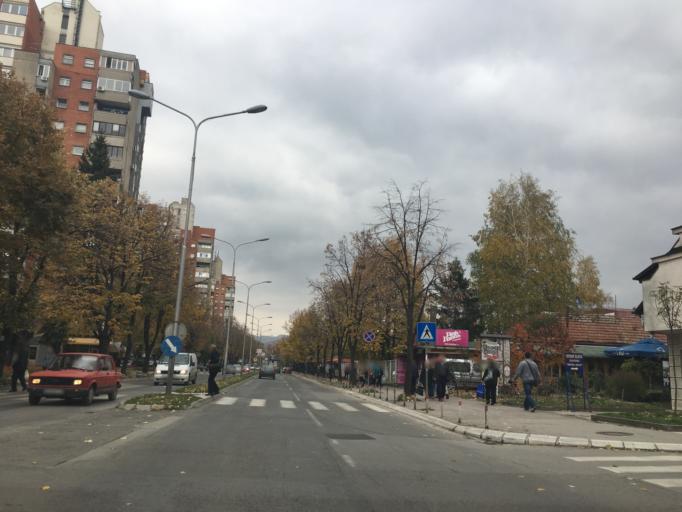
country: RS
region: Central Serbia
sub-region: Raski Okrug
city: Kraljevo
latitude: 43.7229
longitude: 20.6932
